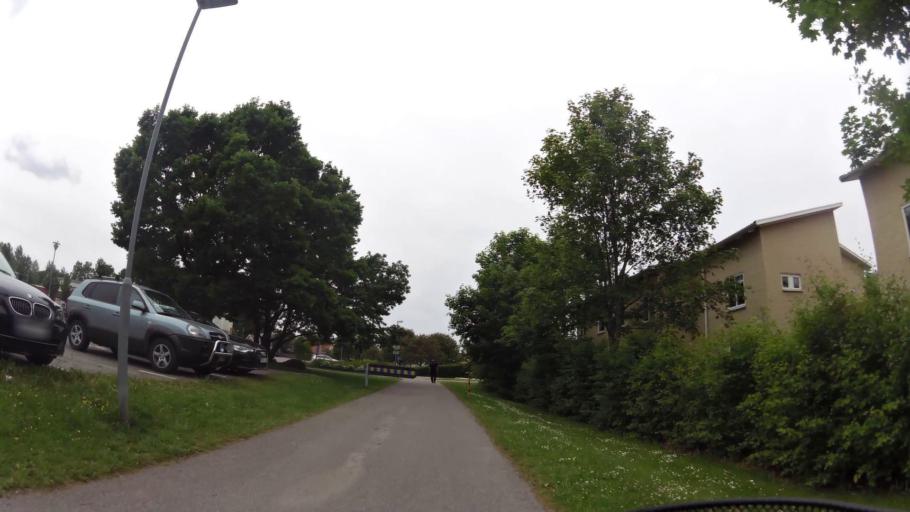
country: SE
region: OEstergoetland
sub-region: Linkopings Kommun
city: Malmslatt
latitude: 58.3871
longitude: 15.5652
